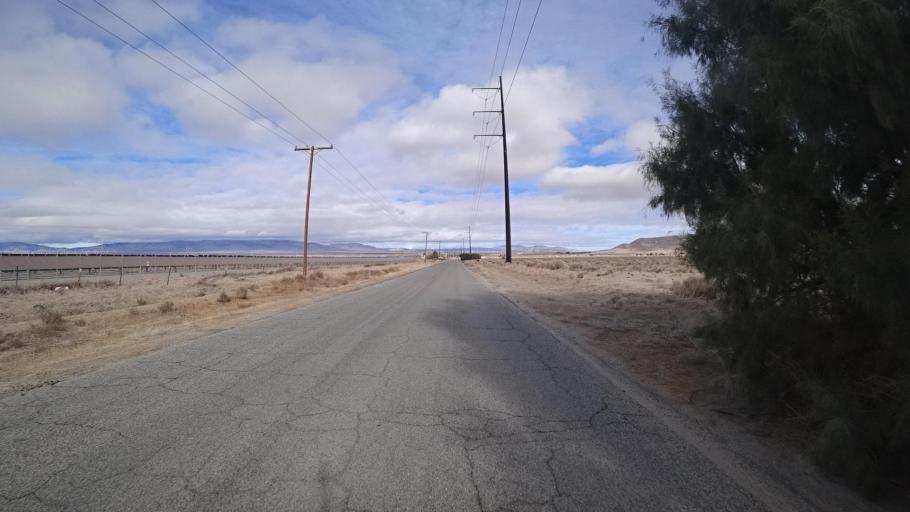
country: US
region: California
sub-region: Kern County
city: Rosamond
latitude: 34.8459
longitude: -118.3088
